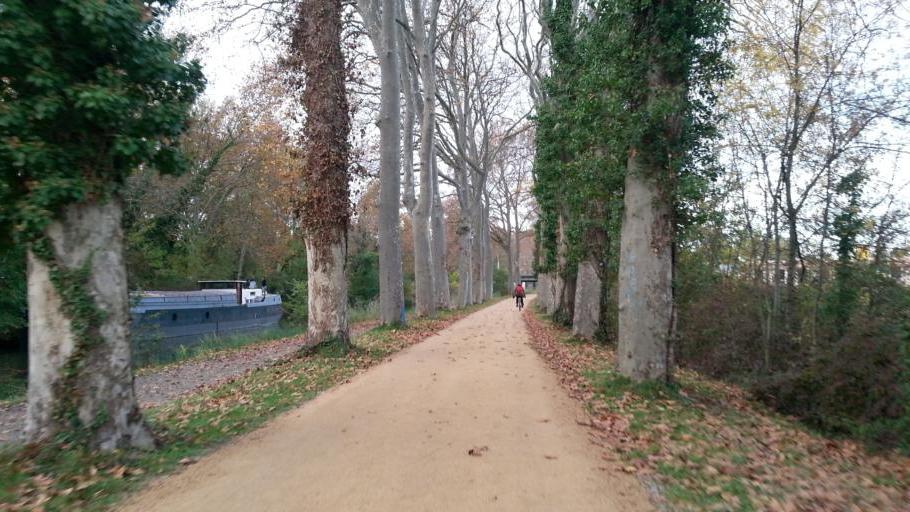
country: FR
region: Midi-Pyrenees
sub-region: Departement de la Haute-Garonne
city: Ramonville-Saint-Agne
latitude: 43.5507
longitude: 1.4824
